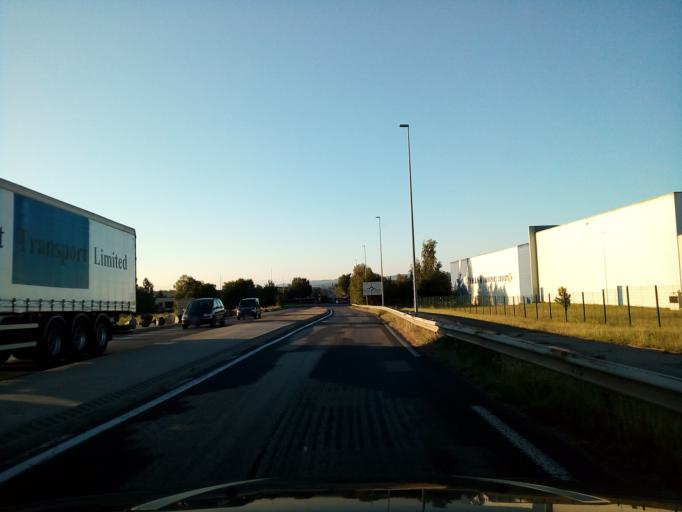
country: FR
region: Rhone-Alpes
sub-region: Departement de l'Isere
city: La Verpilliere
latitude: 45.6452
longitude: 5.1310
